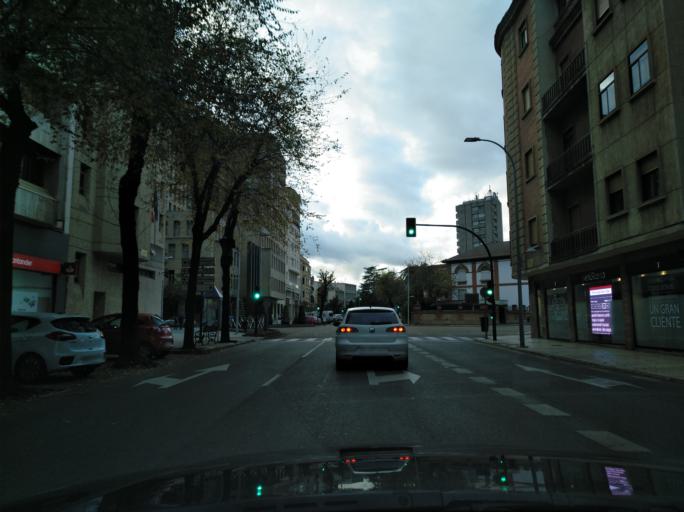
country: ES
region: Extremadura
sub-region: Provincia de Badajoz
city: Badajoz
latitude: 38.8752
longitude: -6.9720
